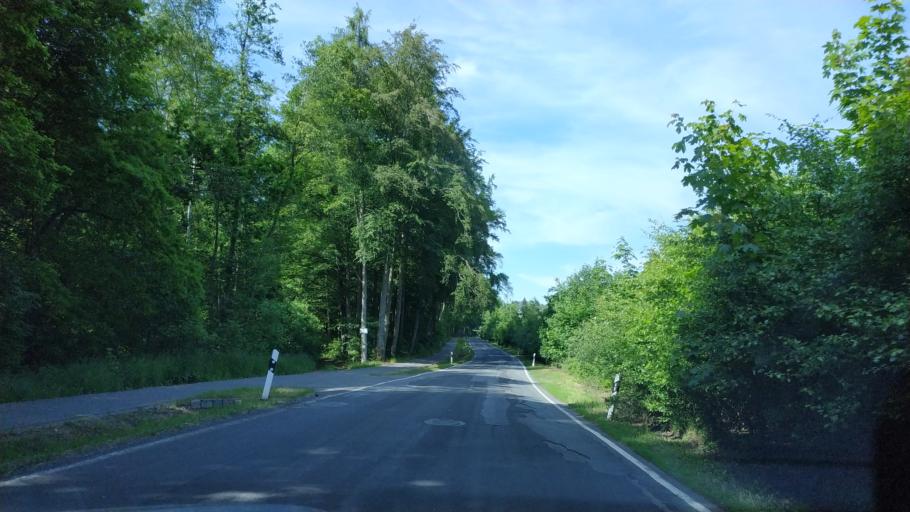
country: DE
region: Saxony
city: Plauen
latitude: 50.5297
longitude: 12.1343
